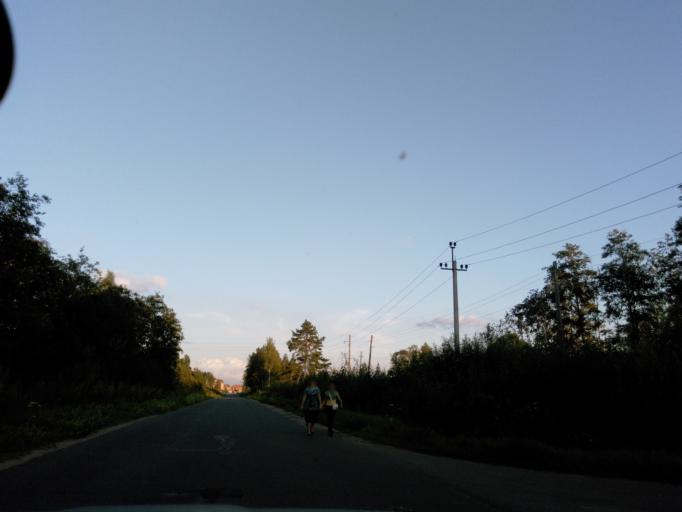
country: RU
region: Tverskaya
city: Konakovo
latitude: 56.6824
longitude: 36.7033
